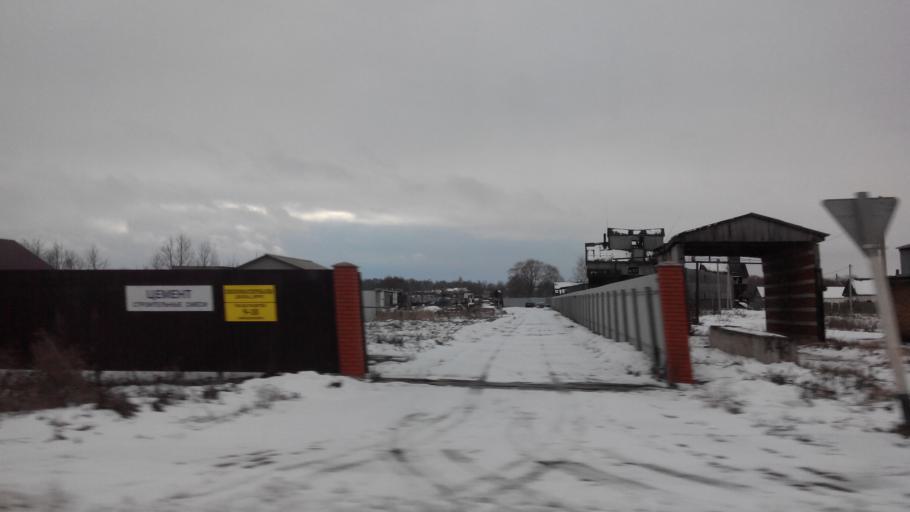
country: RU
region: Tula
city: Mayskiy
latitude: 53.9764
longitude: 38.2380
